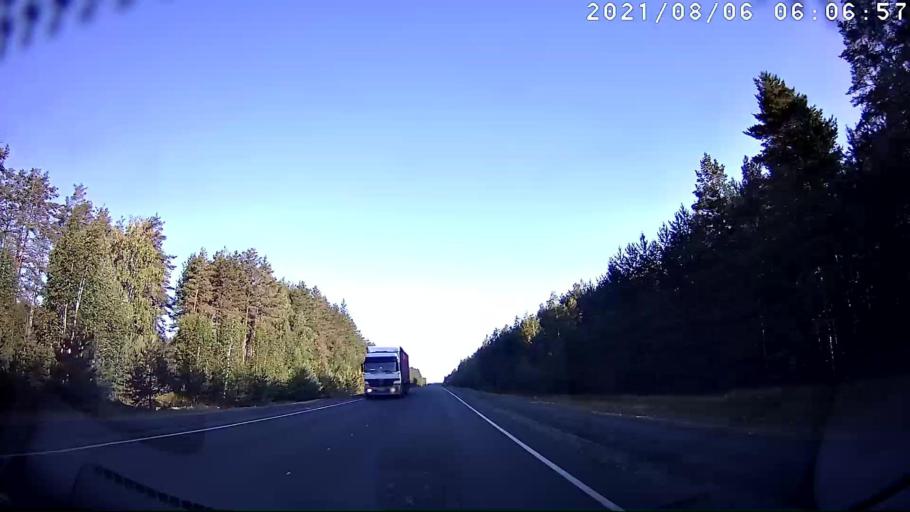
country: RU
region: Mariy-El
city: Volzhsk
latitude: 55.9008
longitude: 48.3856
